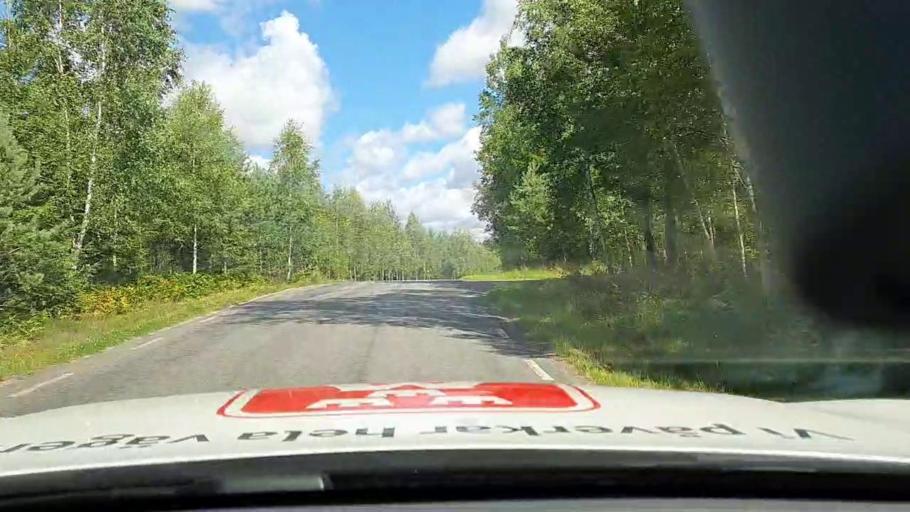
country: SE
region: Vaestra Goetaland
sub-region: Toreboda Kommun
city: Toereboda
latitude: 58.5694
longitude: 14.0453
